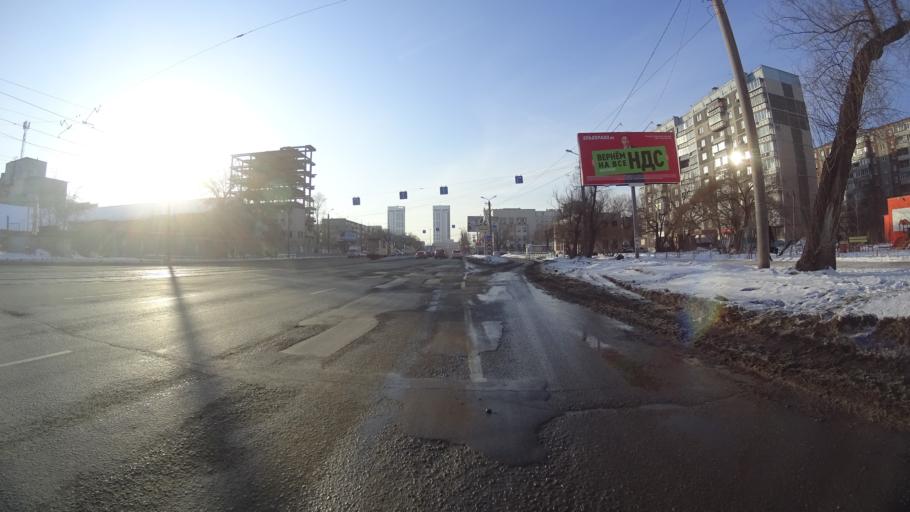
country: RU
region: Chelyabinsk
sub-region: Gorod Chelyabinsk
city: Chelyabinsk
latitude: 55.1682
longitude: 61.4231
